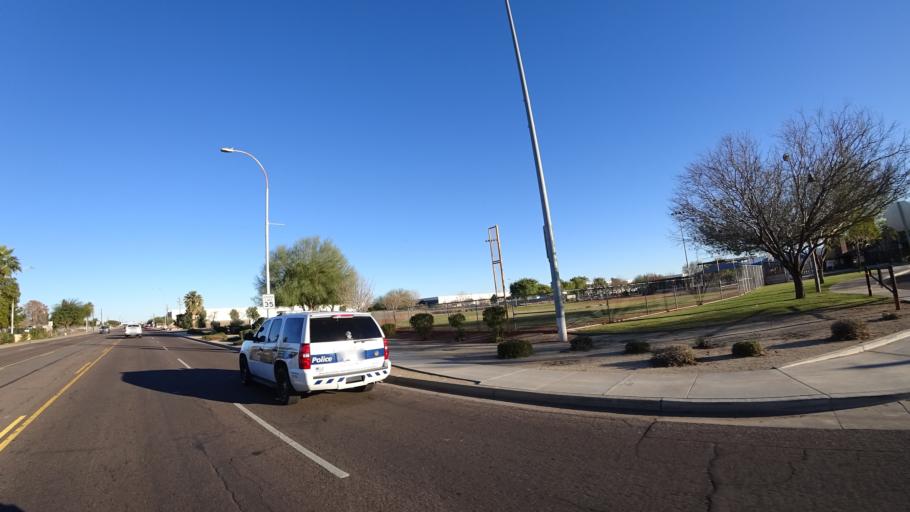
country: US
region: Arizona
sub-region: Maricopa County
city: Tolleson
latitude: 33.4512
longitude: -112.2453
